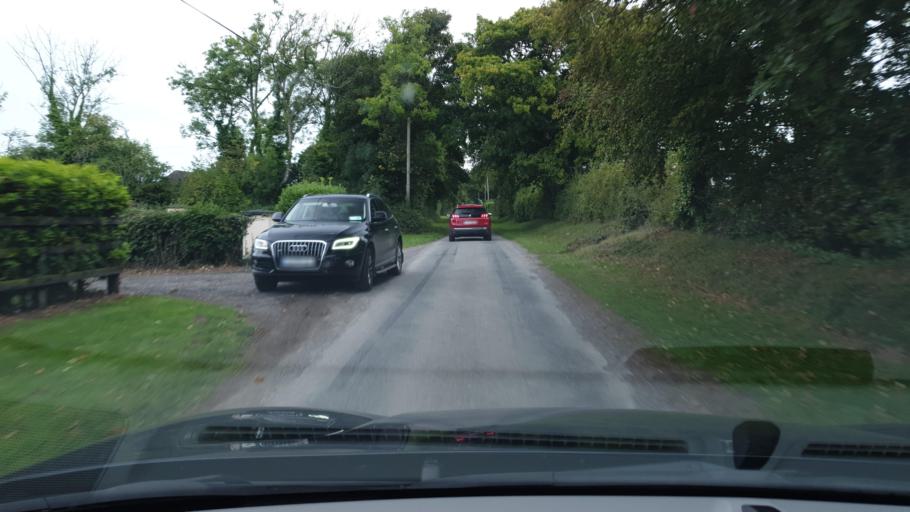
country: IE
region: Leinster
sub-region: An Mhi
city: Dunshaughlin
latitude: 53.5251
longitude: -6.5060
